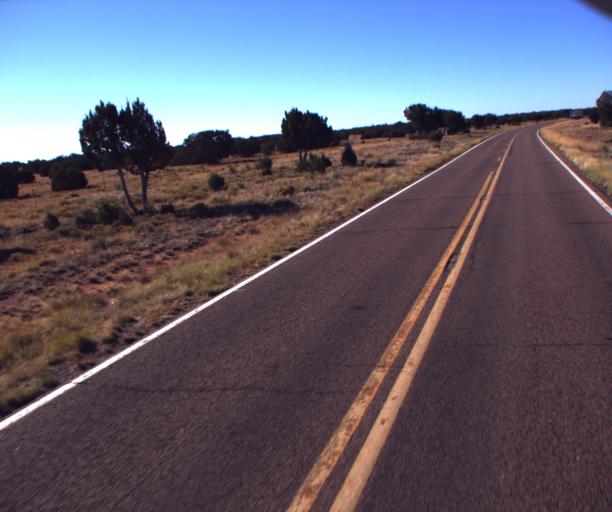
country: US
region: Arizona
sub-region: Navajo County
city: Heber-Overgaard
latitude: 34.5272
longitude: -110.4272
